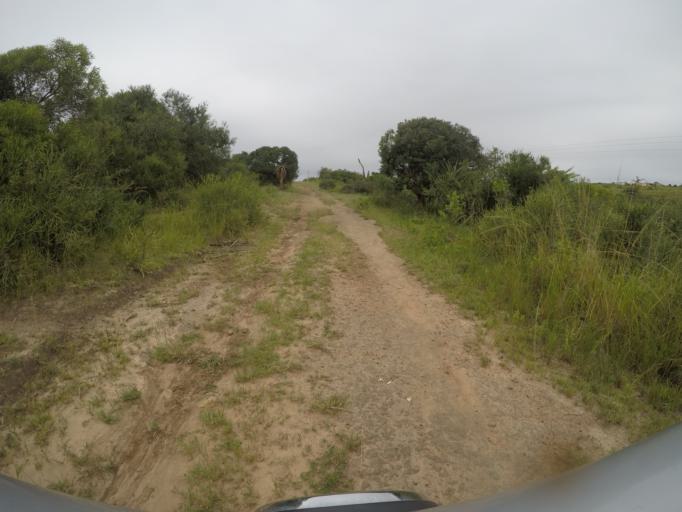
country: ZA
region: KwaZulu-Natal
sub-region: uThungulu District Municipality
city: Empangeni
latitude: -28.6071
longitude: 31.8377
